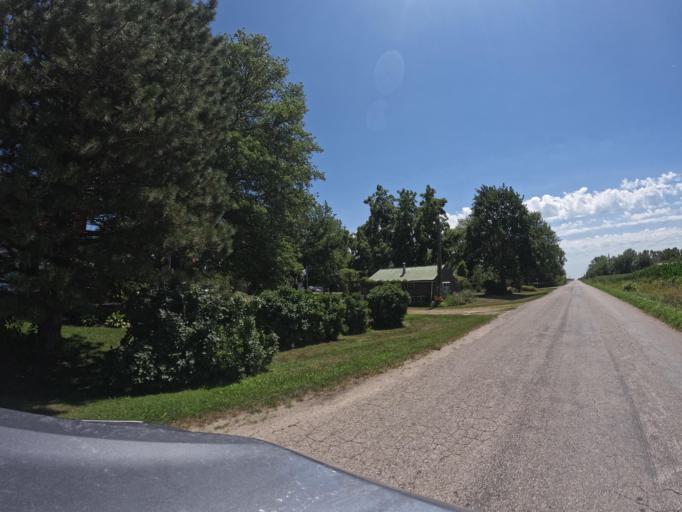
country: US
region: Iowa
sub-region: Keokuk County
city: Sigourney
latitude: 41.4548
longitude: -92.3357
